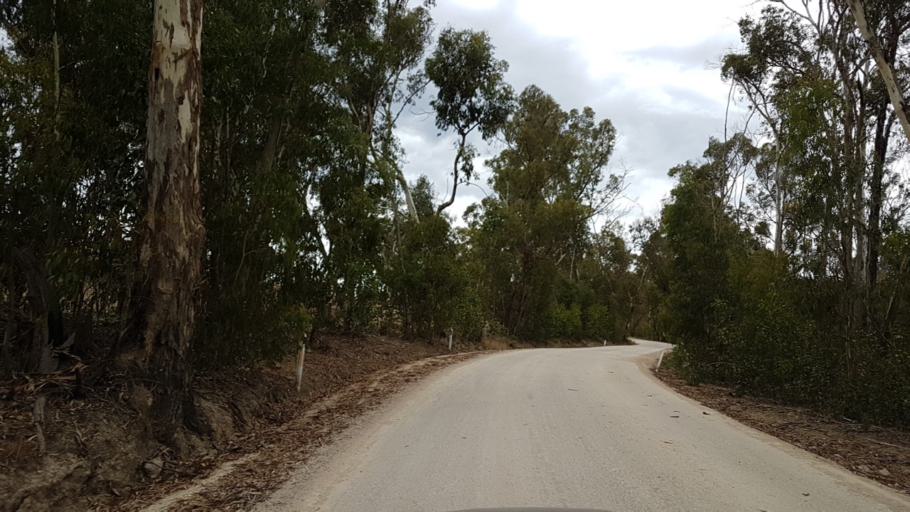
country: AU
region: South Australia
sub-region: Adelaide Hills
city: Gumeracha
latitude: -34.7859
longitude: 138.8372
